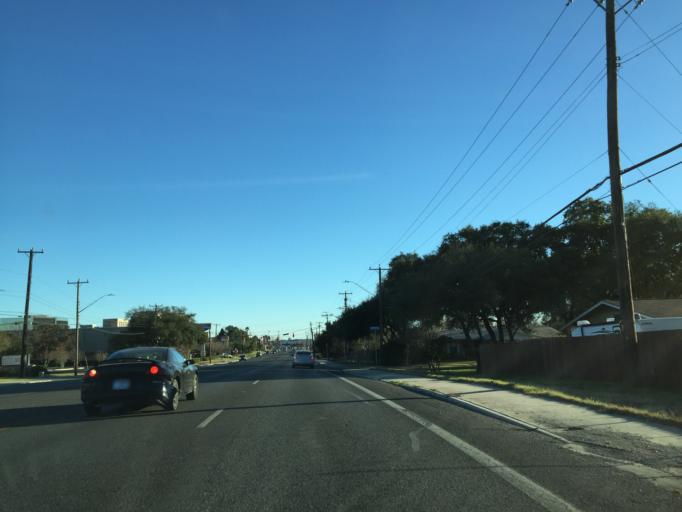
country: US
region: Texas
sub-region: Bexar County
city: Castle Hills
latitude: 29.5282
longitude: -98.5055
